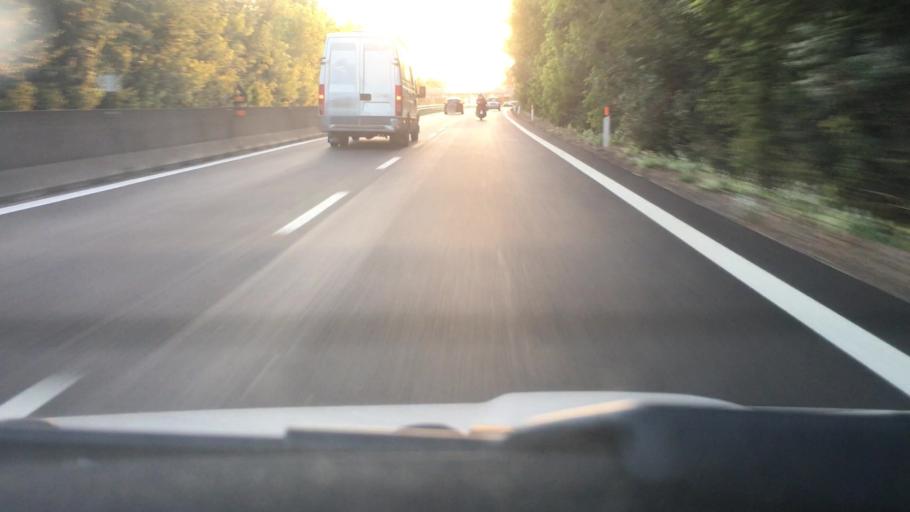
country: IT
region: Emilia-Romagna
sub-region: Provincia di Ferrara
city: Quartesana
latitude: 44.7857
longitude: 11.7387
